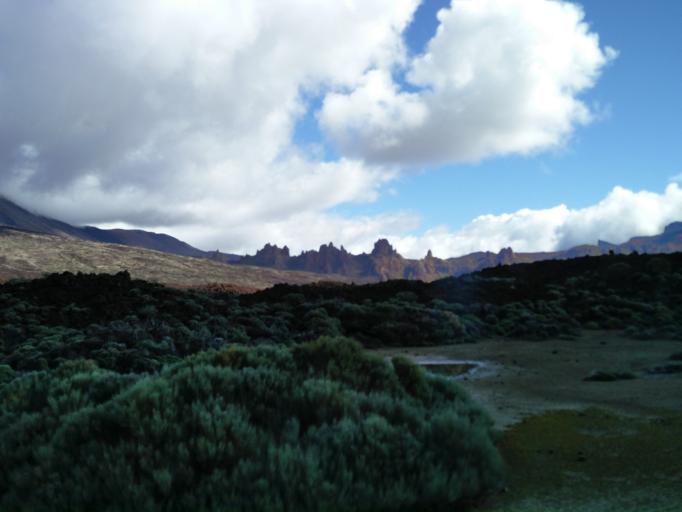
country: ES
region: Canary Islands
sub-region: Provincia de Santa Cruz de Tenerife
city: Vilaflor
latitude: 28.2124
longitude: -16.6599
